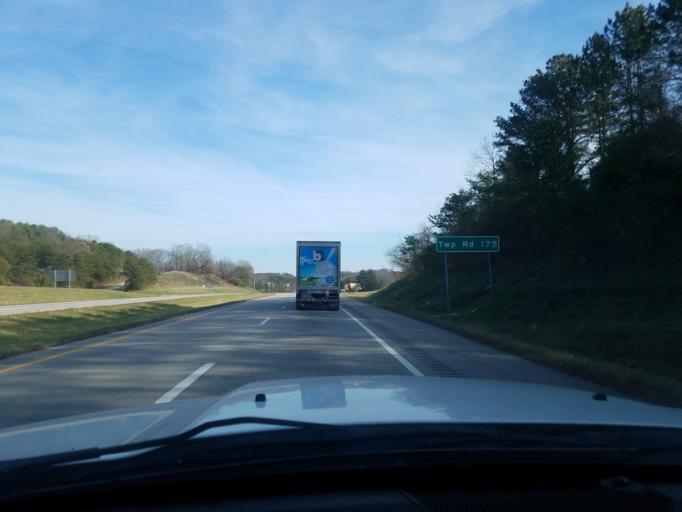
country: US
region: West Virginia
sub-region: Wood County
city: Washington
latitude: 39.2363
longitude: -81.7777
